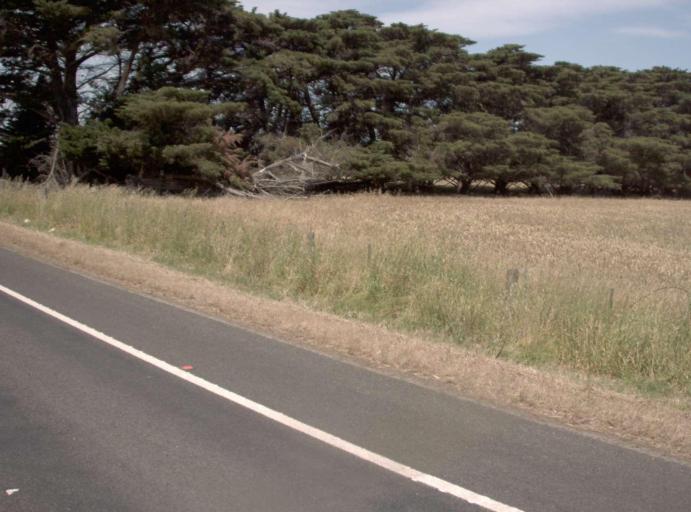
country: AU
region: Victoria
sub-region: Wellington
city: Heyfield
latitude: -38.1213
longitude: 146.8542
